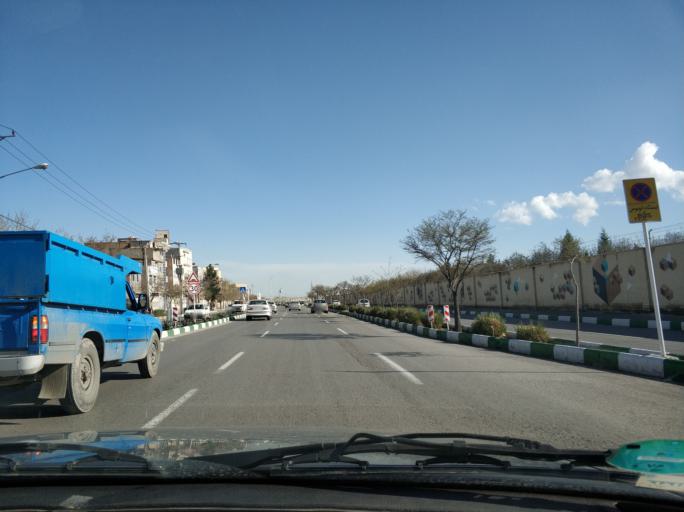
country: IR
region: Razavi Khorasan
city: Mashhad
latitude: 36.3093
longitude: 59.6248
